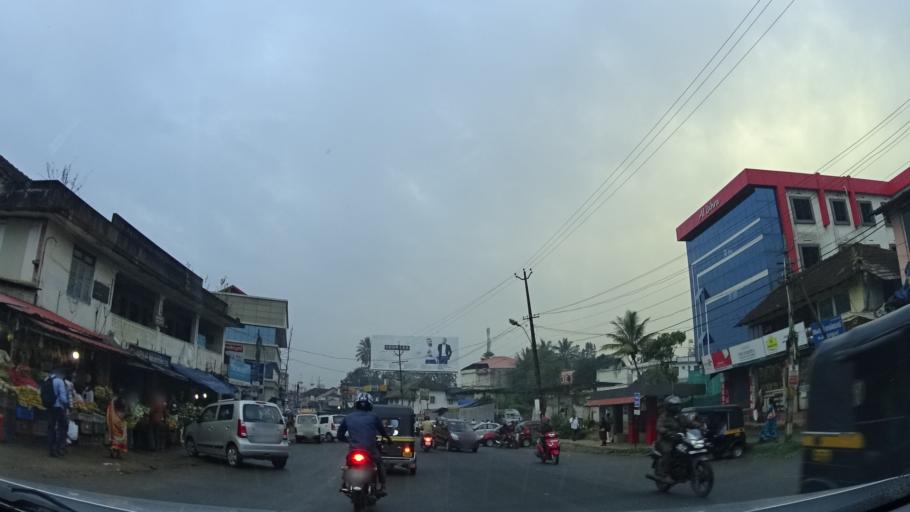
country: IN
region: Kerala
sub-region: Wayanad
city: Kalpetta
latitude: 11.6089
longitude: 76.0834
